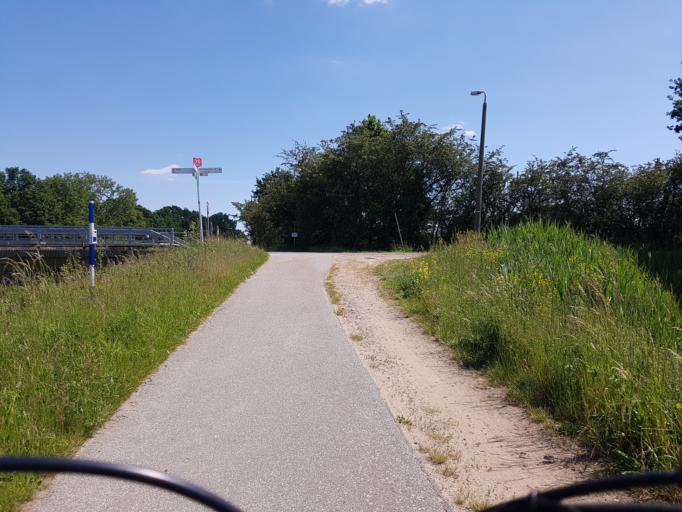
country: DE
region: Brandenburg
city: Elsterwerda
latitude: 51.4780
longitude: 13.4626
